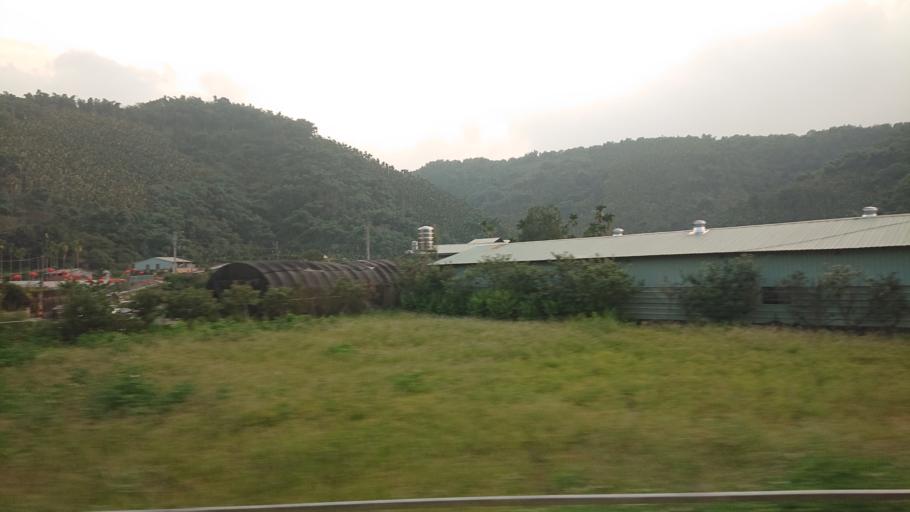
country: TW
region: Taiwan
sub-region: Nantou
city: Puli
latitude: 23.9689
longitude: 120.9979
